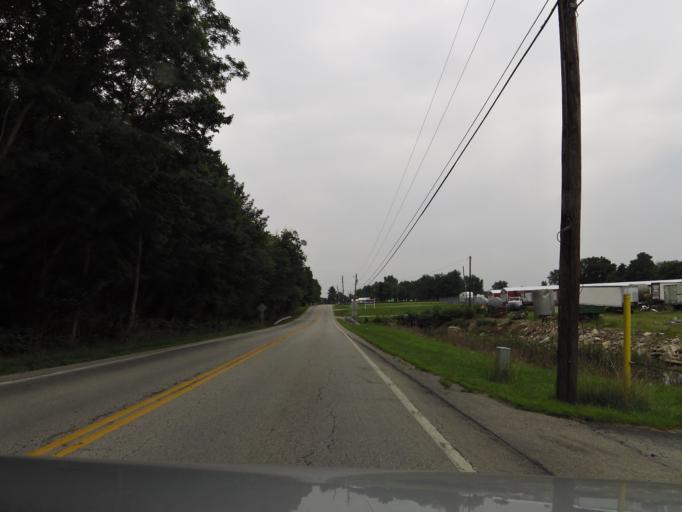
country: US
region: Ohio
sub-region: Brown County
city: Mount Orab
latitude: 39.1593
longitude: -83.9324
